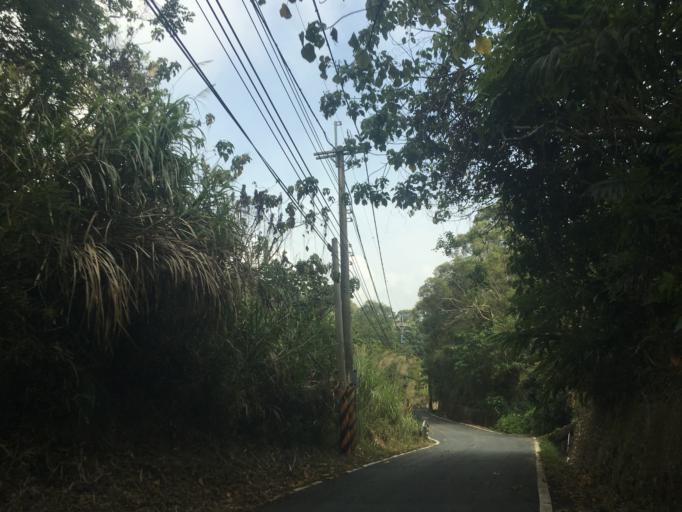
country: TW
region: Taiwan
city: Fengyuan
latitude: 24.2211
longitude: 120.7619
